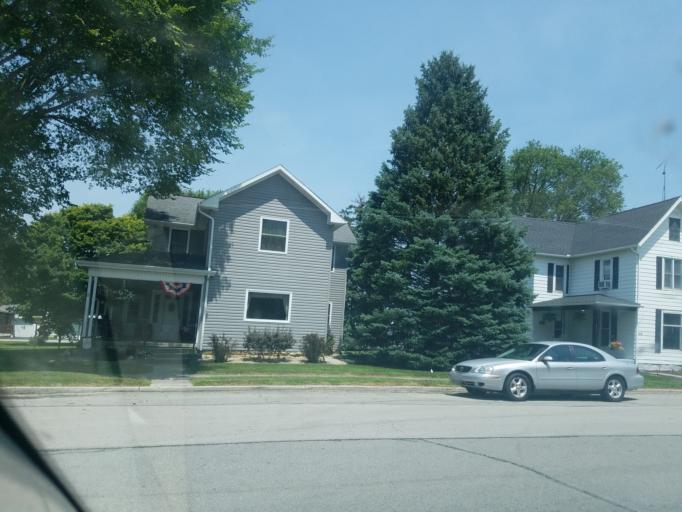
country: US
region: Ohio
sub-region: Wyandot County
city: Carey
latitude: 40.9759
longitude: -83.4812
